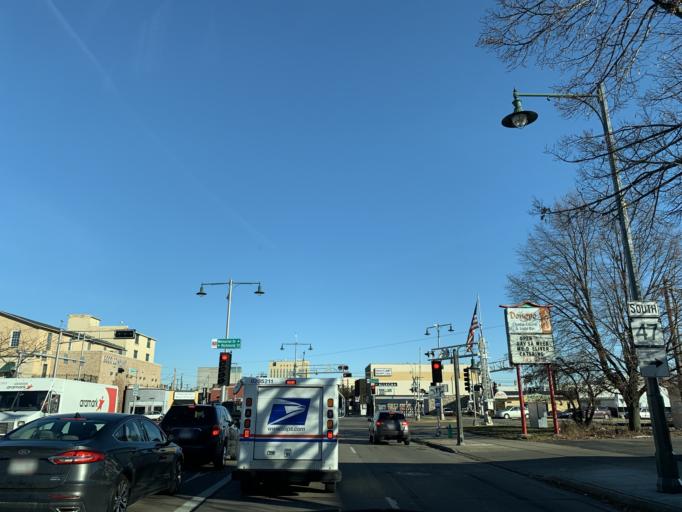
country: US
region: Wisconsin
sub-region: Outagamie County
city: Appleton
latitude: 44.2618
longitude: -88.4164
